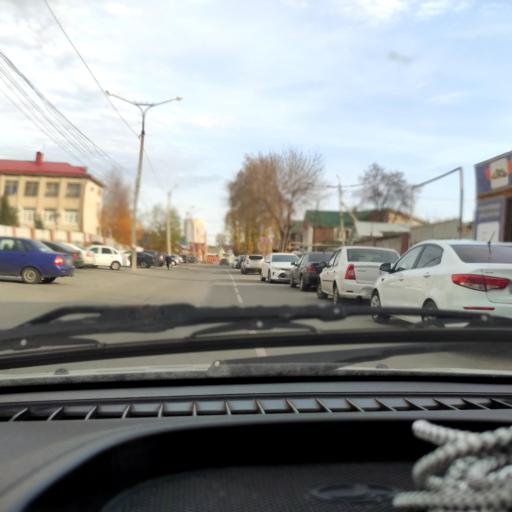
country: RU
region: Samara
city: Tol'yatti
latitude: 53.5239
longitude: 49.4062
